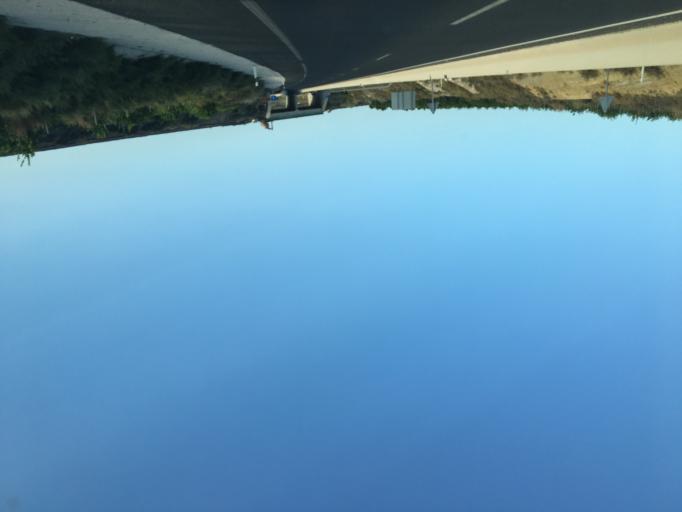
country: ES
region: Murcia
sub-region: Murcia
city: Beniel
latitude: 37.9900
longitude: -0.9745
